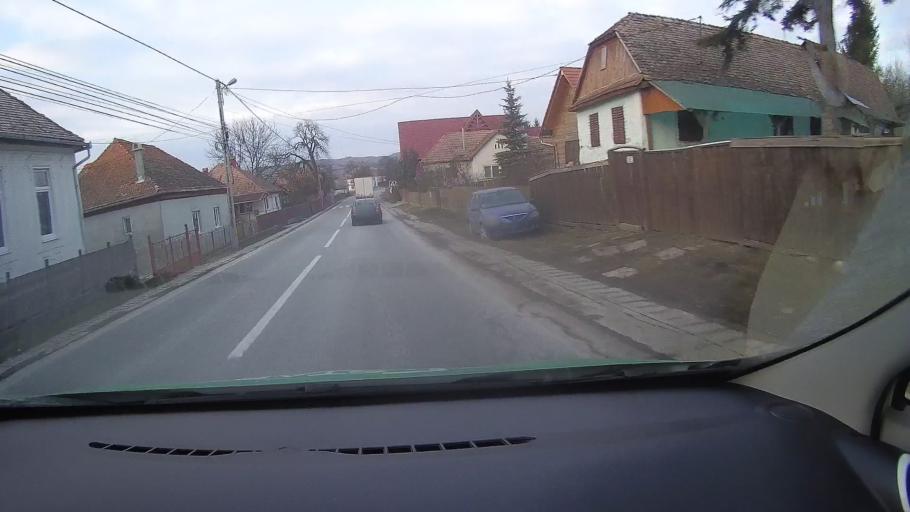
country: RO
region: Harghita
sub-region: Comuna Simonesti
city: Simonesti
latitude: 46.3339
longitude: 25.1069
